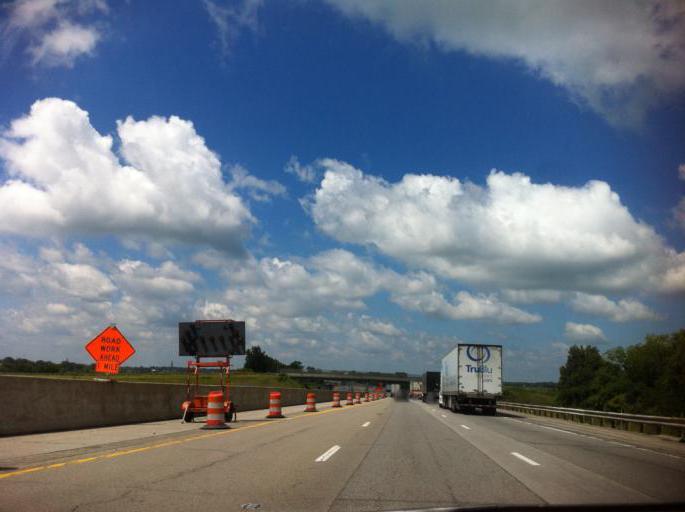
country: US
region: Ohio
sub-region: Huron County
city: Bellevue
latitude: 41.3458
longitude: -82.7908
